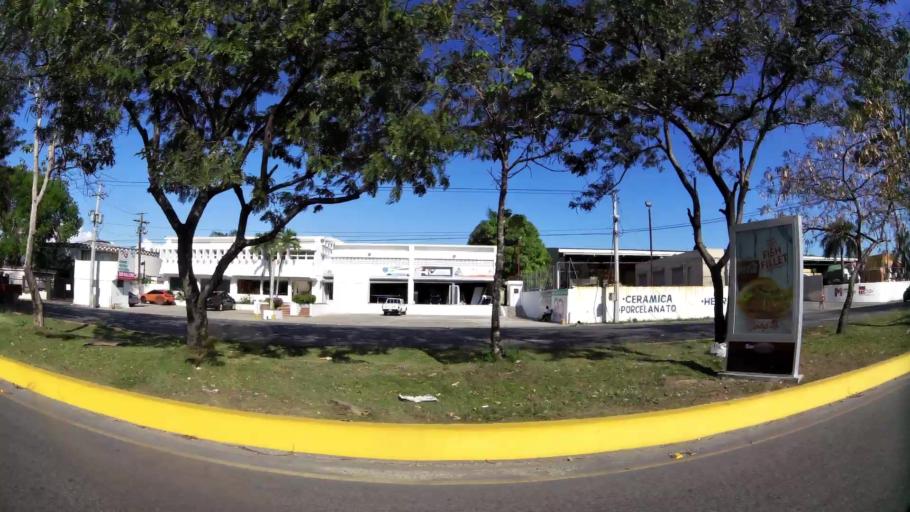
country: DO
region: Nacional
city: Bella Vista
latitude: 18.4718
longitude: -69.9682
